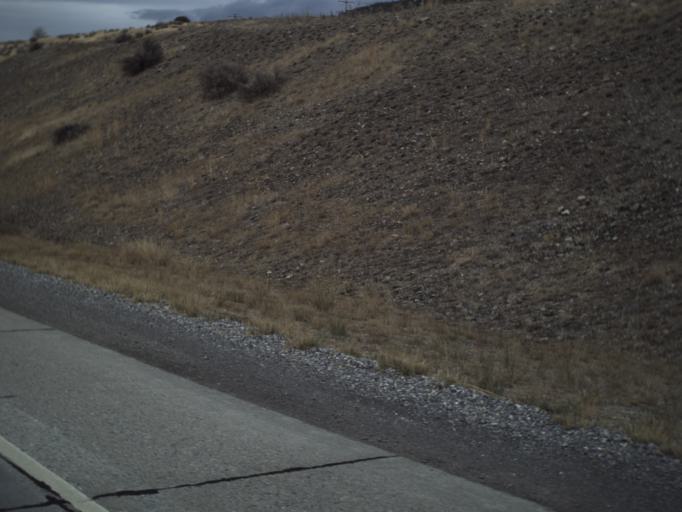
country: US
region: Idaho
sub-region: Oneida County
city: Malad City
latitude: 41.9753
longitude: -112.1880
